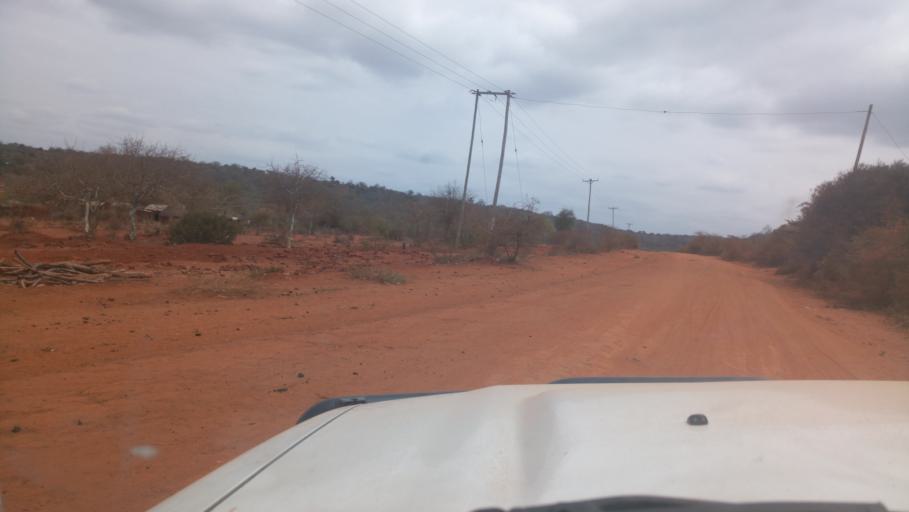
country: KE
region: Makueni
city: Wote
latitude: -1.8818
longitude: 37.9723
